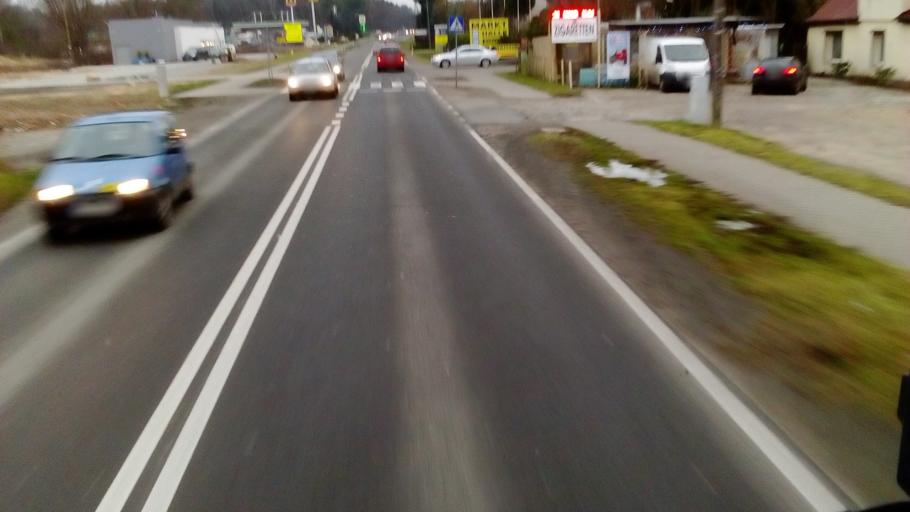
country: PL
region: West Pomeranian Voivodeship
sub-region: Powiat policki
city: Dobra
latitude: 53.4493
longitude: 14.3893
